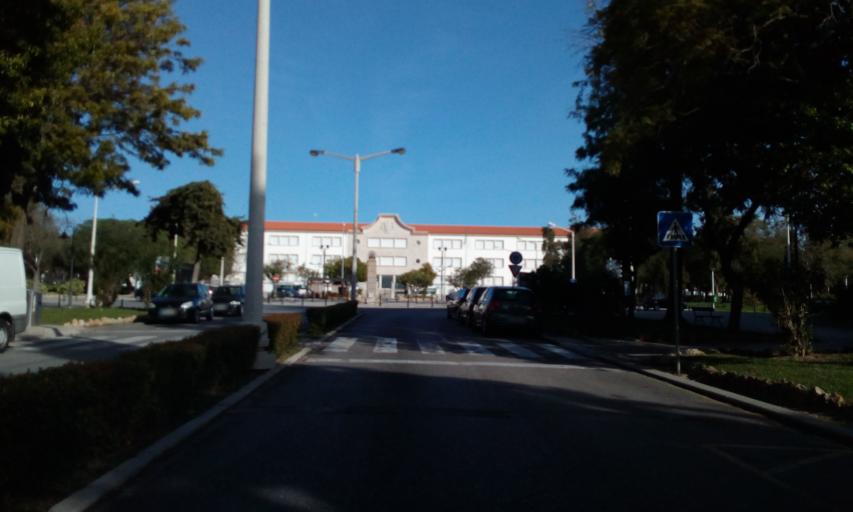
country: PT
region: Faro
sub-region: Faro
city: Faro
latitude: 37.0184
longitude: -7.9236
